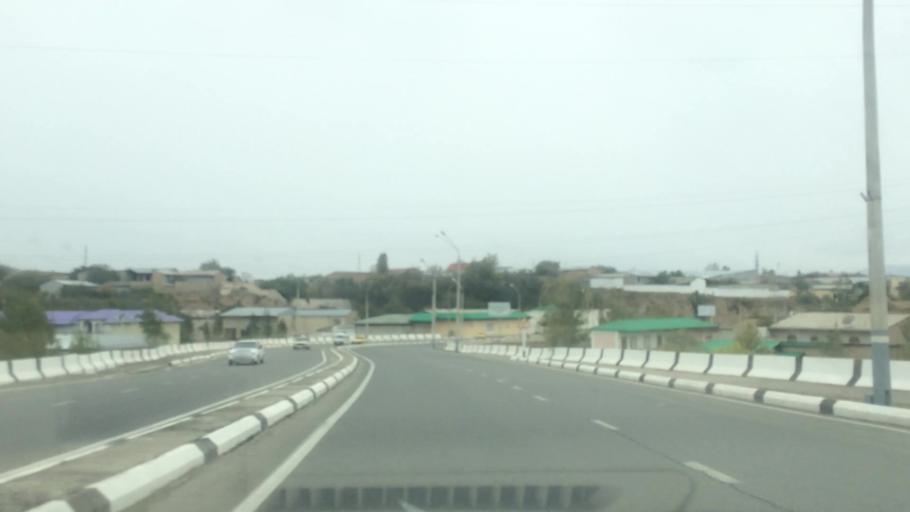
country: UZ
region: Samarqand
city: Samarqand
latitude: 39.6723
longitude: 66.9999
